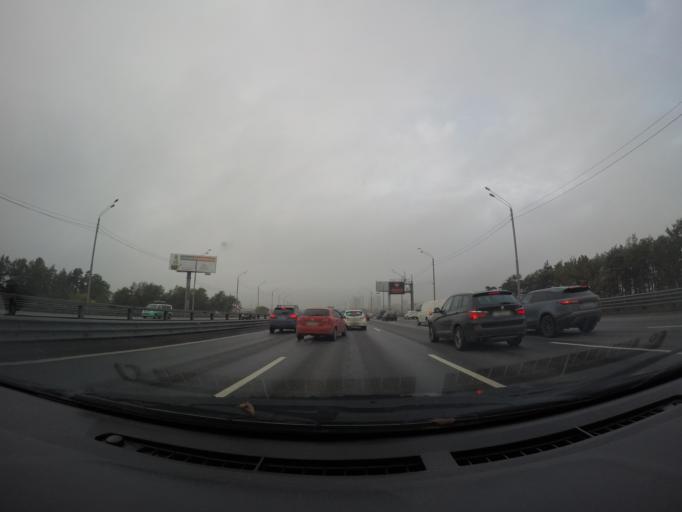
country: RU
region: Moscow
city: Rublevo
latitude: 55.7987
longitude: 37.3435
